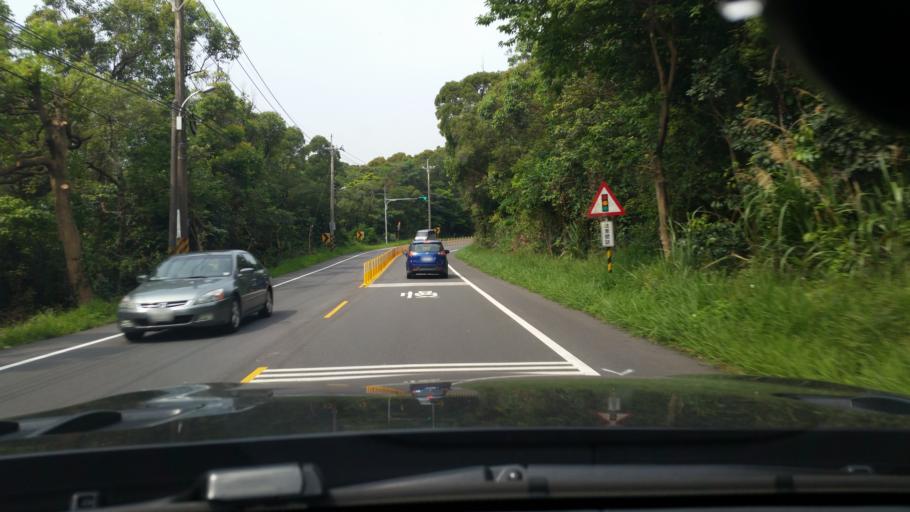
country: TW
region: Taiwan
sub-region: Taoyuan
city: Taoyuan
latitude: 25.0605
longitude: 121.3312
